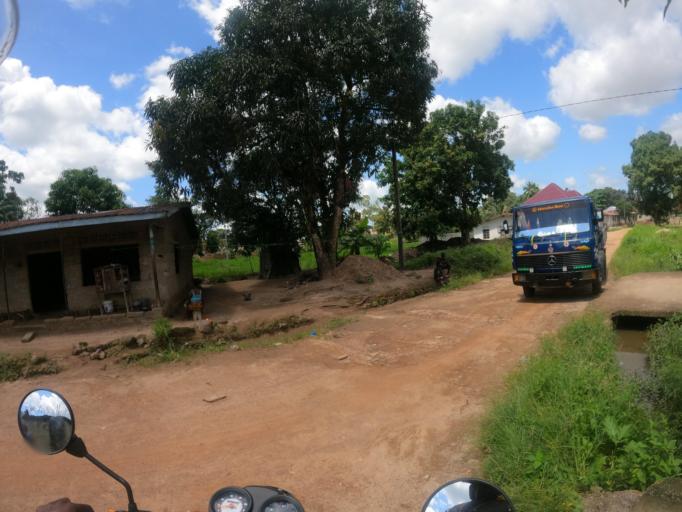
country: SL
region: Northern Province
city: Makeni
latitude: 8.8902
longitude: -12.0647
